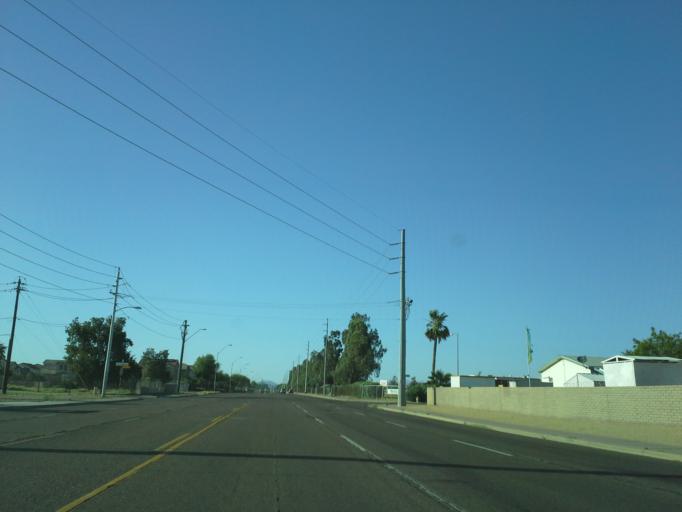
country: US
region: Arizona
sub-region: Maricopa County
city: Glendale
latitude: 33.6285
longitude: -112.0997
